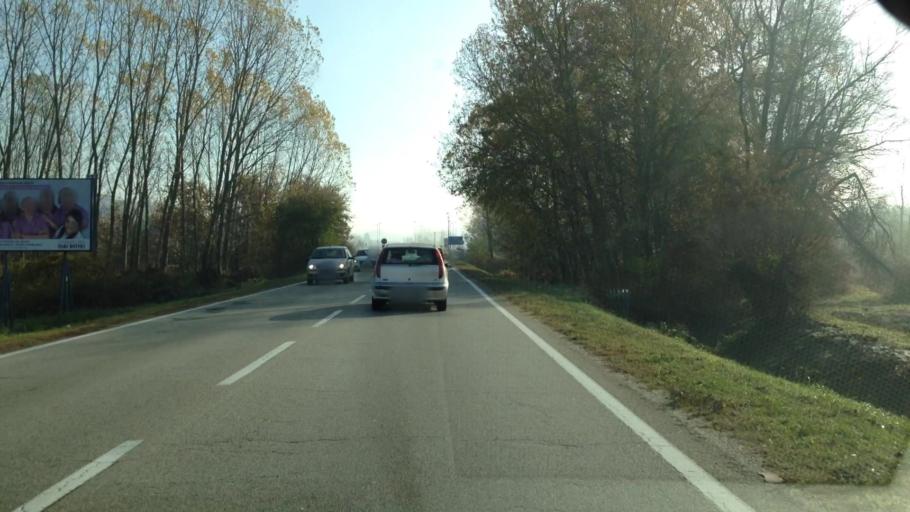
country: IT
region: Piedmont
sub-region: Provincia di Asti
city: Vigliano d'Asti
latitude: 44.8239
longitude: 8.2208
